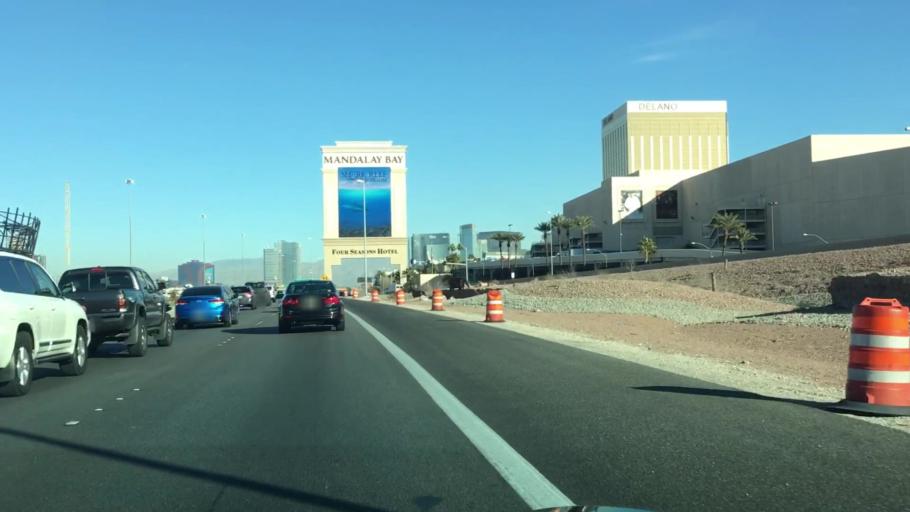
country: US
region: Nevada
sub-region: Clark County
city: Paradise
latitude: 36.0867
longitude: -115.1799
